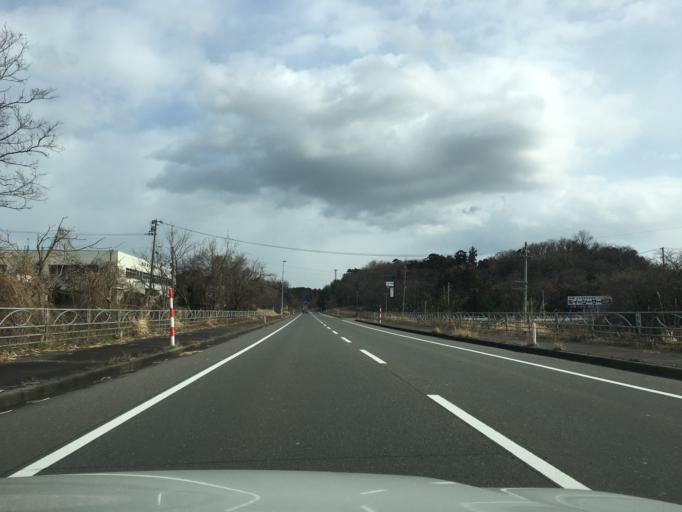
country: JP
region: Yamagata
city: Yuza
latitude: 39.2464
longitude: 139.9230
